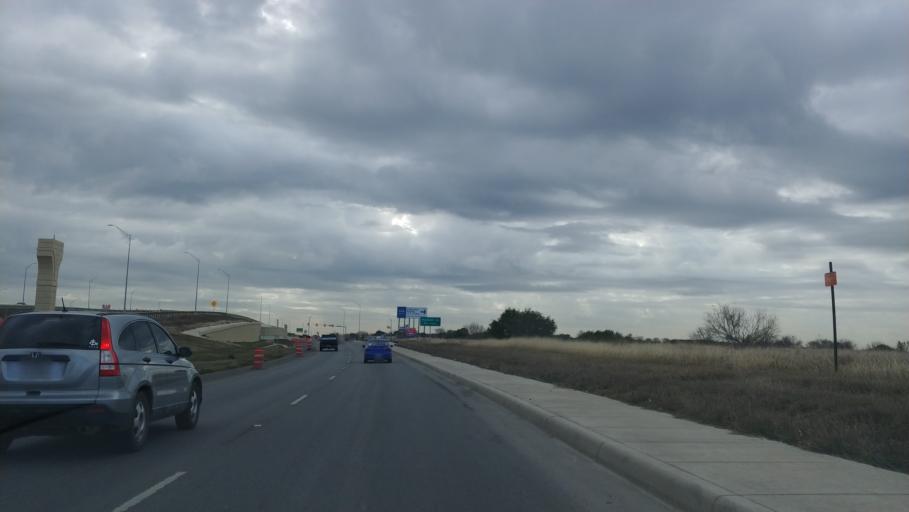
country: US
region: Texas
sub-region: Bexar County
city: Lackland Air Force Base
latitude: 29.4057
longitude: -98.7092
